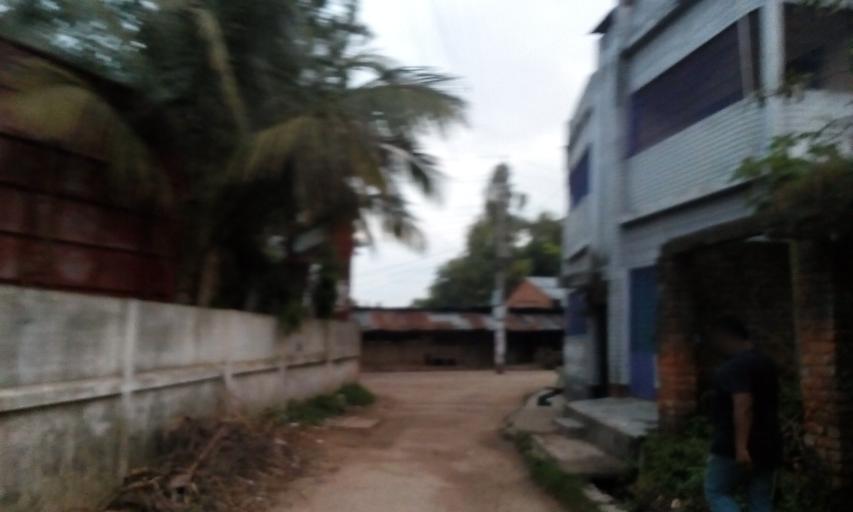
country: IN
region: West Bengal
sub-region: Dakshin Dinajpur
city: Balurghat
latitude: 25.3810
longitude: 88.9931
